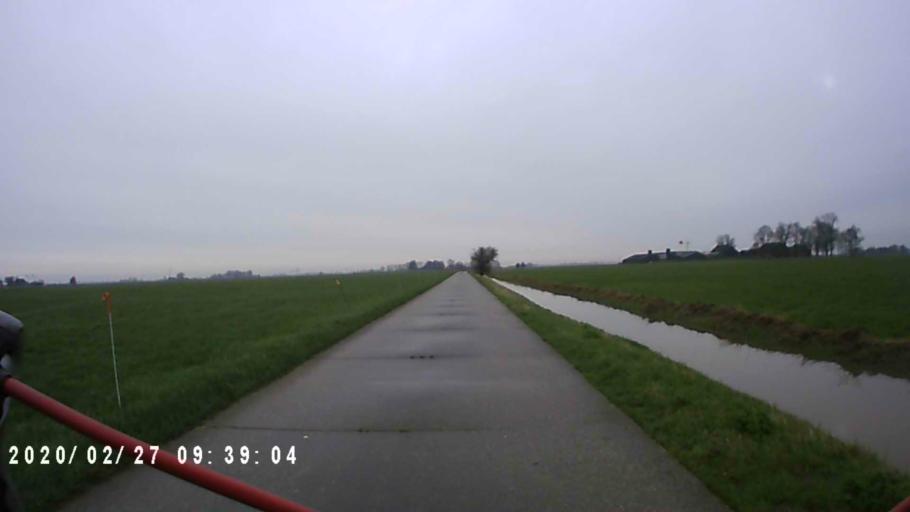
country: NL
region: Groningen
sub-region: Gemeente Zuidhorn
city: Aduard
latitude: 53.2781
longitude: 6.4310
